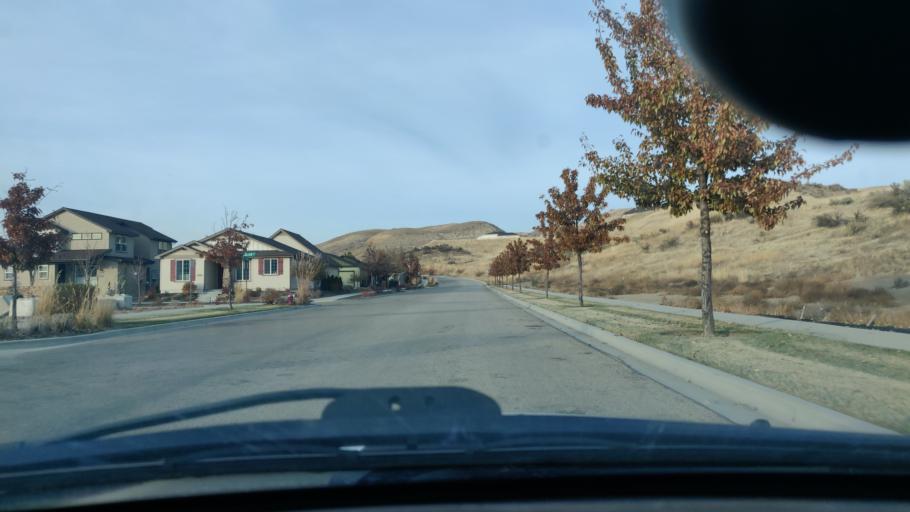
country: US
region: Idaho
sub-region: Ada County
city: Eagle
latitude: 43.7736
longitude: -116.2617
